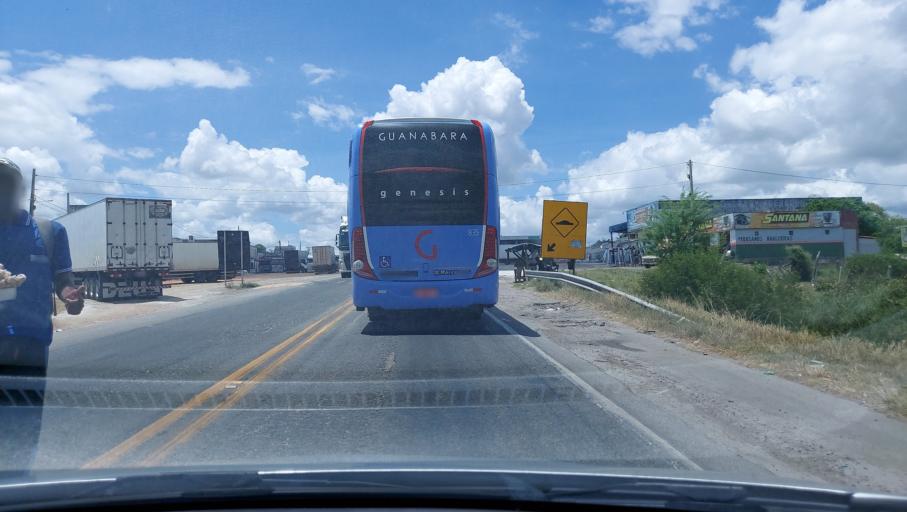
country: BR
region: Bahia
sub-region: Castro Alves
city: Castro Alves
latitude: -12.5810
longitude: -39.5165
